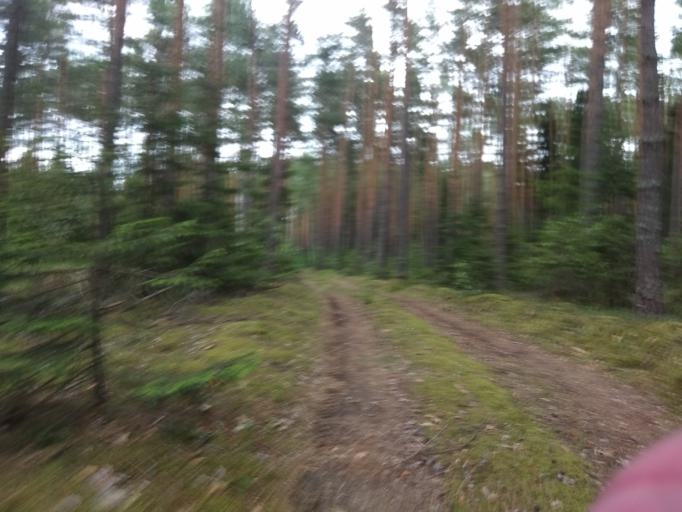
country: RU
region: Moskovskaya
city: Misheronskiy
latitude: 55.6667
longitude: 39.6975
